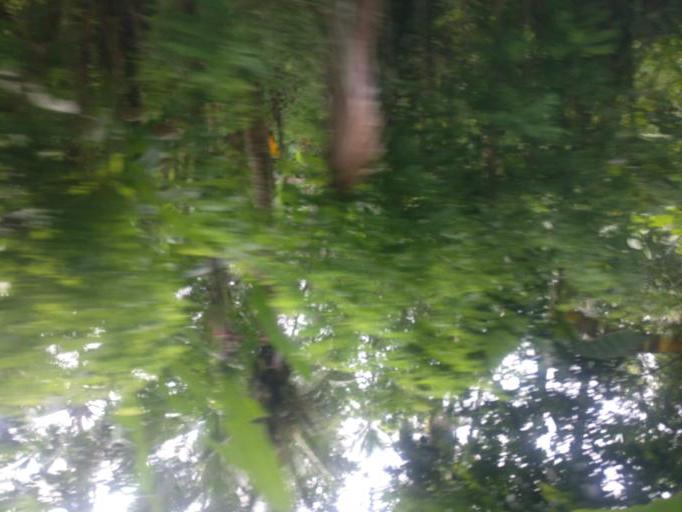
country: ID
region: Bali
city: Banjar Kawan
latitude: -8.4909
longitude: 115.5161
